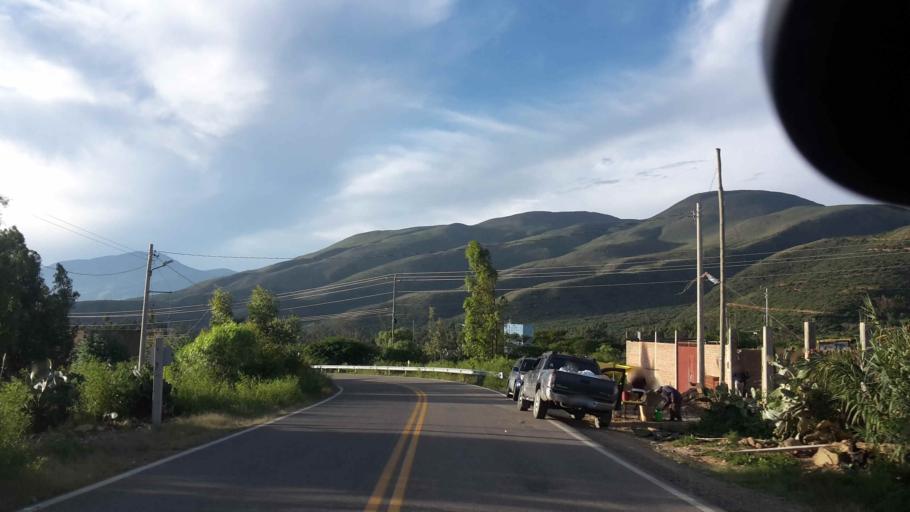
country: BO
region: Cochabamba
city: Arani
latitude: -17.5761
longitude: -65.7589
